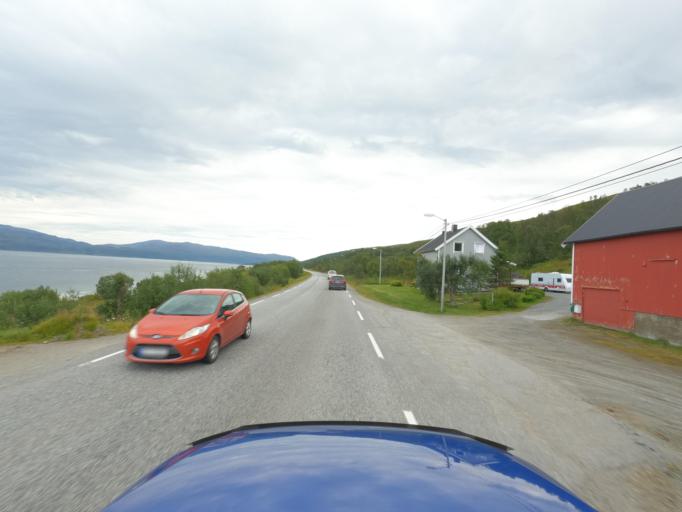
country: NO
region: Finnmark Fylke
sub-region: Kvalsund
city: Kvalsund
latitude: 70.4996
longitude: 24.0715
